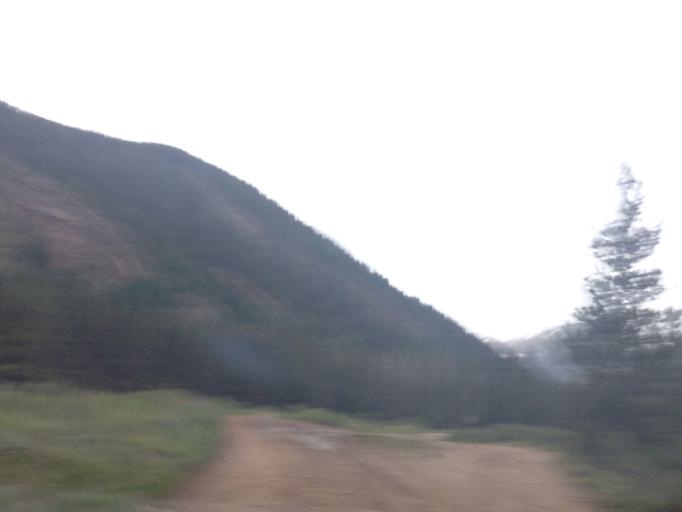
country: US
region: Colorado
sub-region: Clear Creek County
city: Georgetown
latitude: 39.5577
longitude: -105.7599
